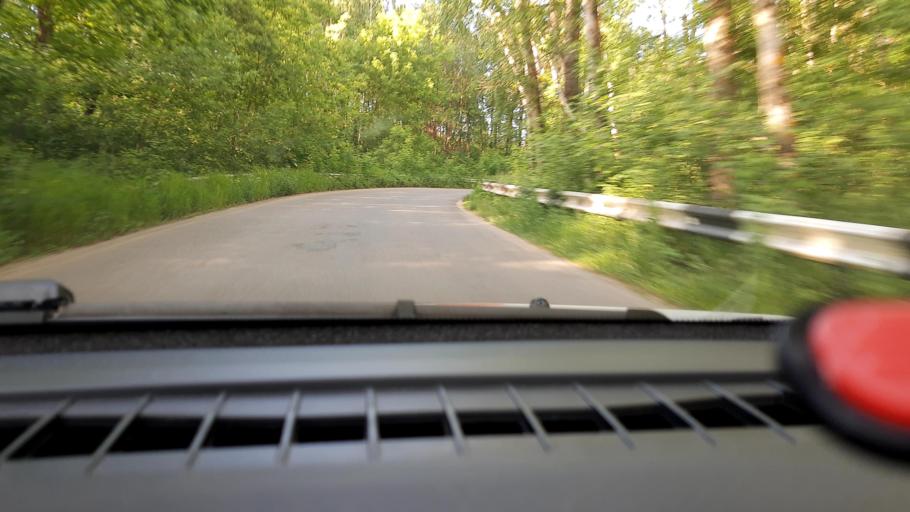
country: RU
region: Nizjnij Novgorod
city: Gorbatovka
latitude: 56.2242
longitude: 43.7571
